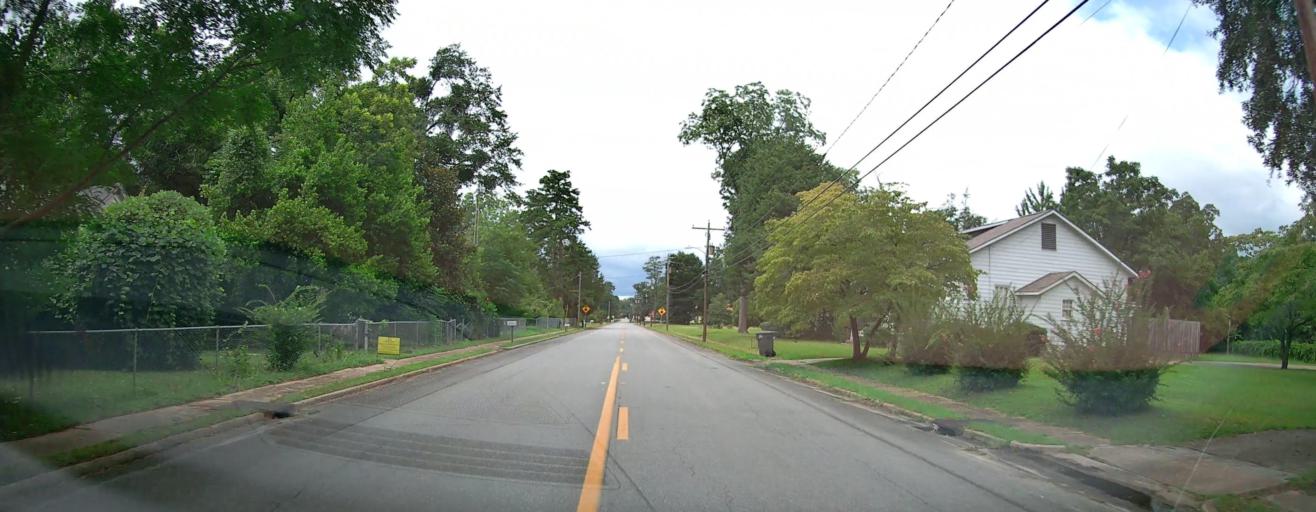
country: US
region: Georgia
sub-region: Twiggs County
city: Jeffersonville
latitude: 32.6851
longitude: -83.3396
